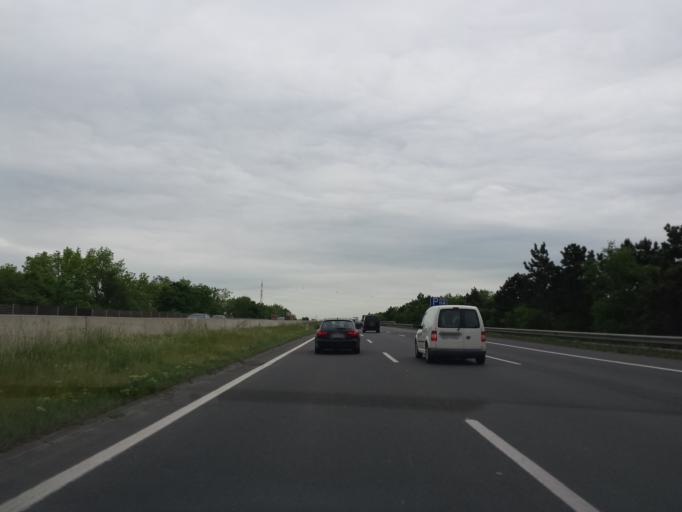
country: AT
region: Lower Austria
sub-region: Politischer Bezirk Baden
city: Leobersdorf
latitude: 47.9221
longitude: 16.2086
